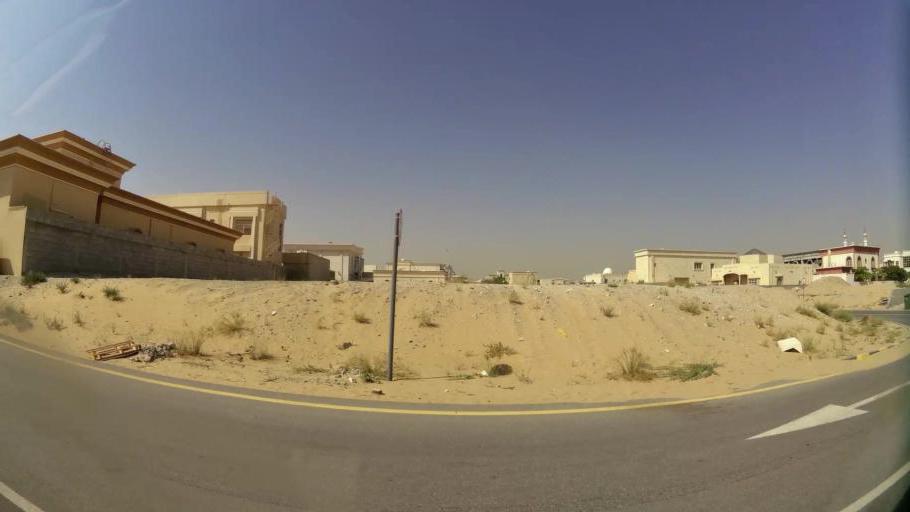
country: AE
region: Ajman
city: Ajman
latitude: 25.4132
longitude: 55.5415
